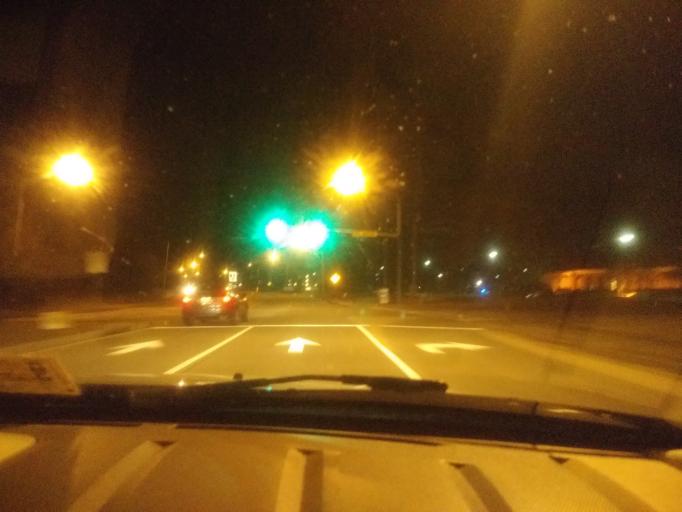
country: US
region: Virginia
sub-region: City of Chesapeake
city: Chesapeake
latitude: 36.7996
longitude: -76.1900
